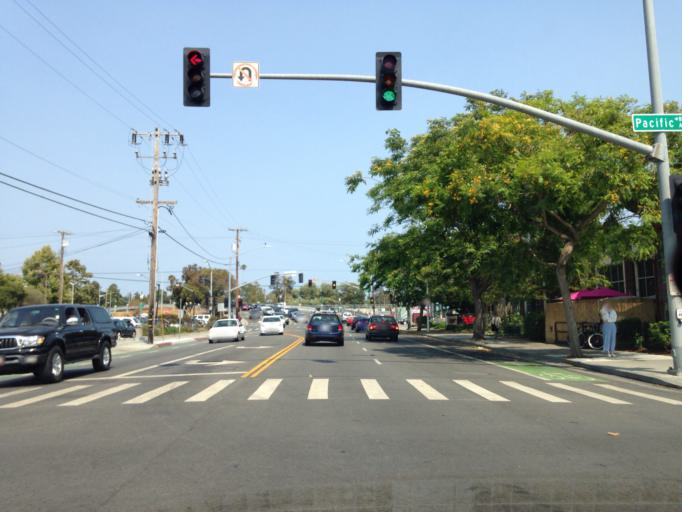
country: US
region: California
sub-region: Santa Cruz County
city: Santa Cruz
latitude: 36.9692
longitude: -122.0249
